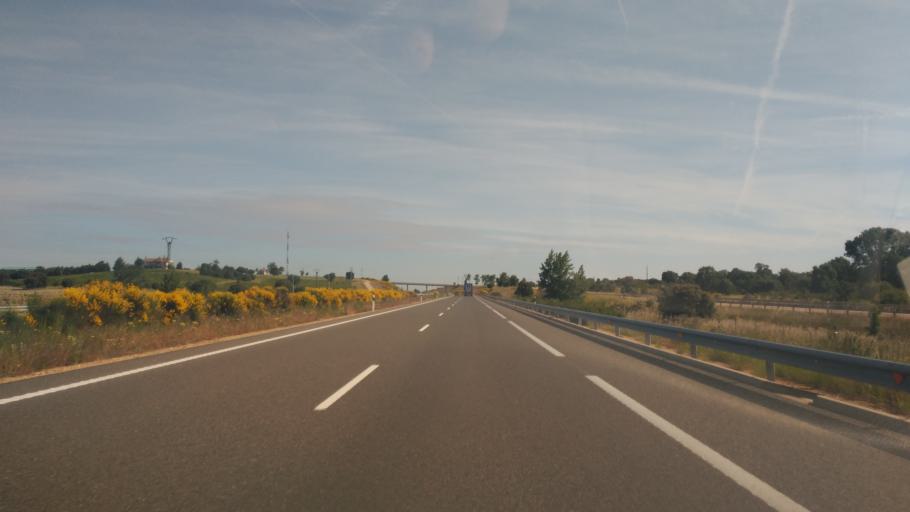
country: ES
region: Castille and Leon
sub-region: Provincia de Salamanca
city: Topas
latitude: 41.1732
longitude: -5.6951
